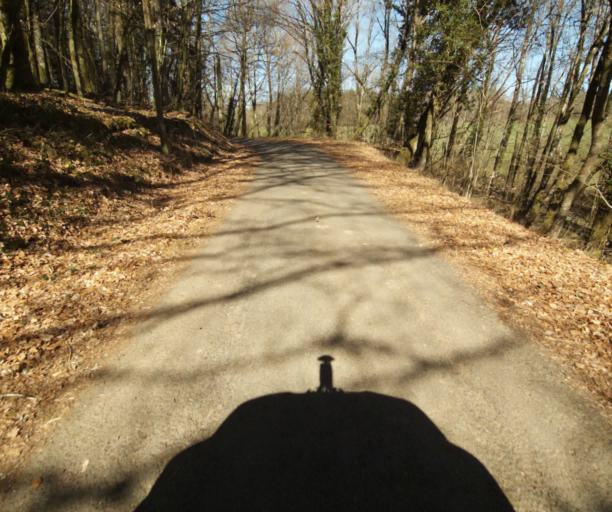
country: FR
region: Limousin
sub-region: Departement de la Correze
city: Chamboulive
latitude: 45.4176
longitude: 1.7192
